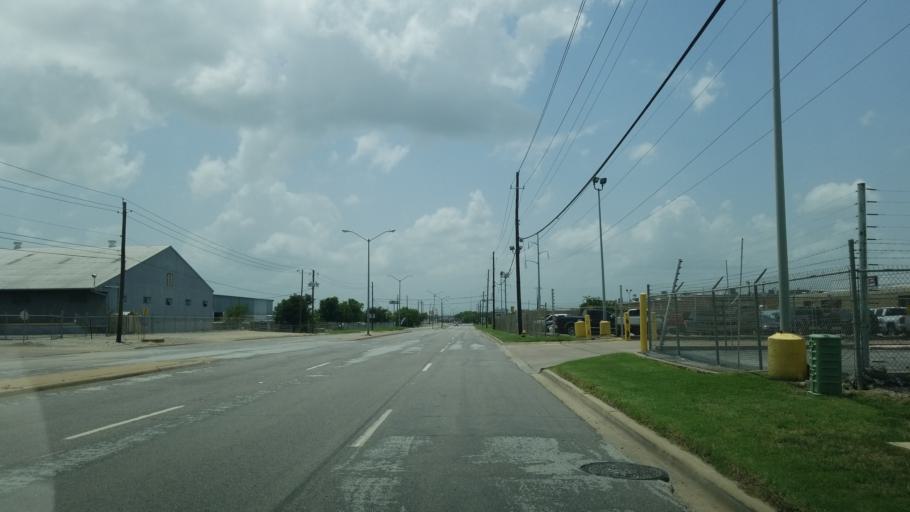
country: US
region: Texas
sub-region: Dallas County
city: Cockrell Hill
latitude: 32.7790
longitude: -96.8844
